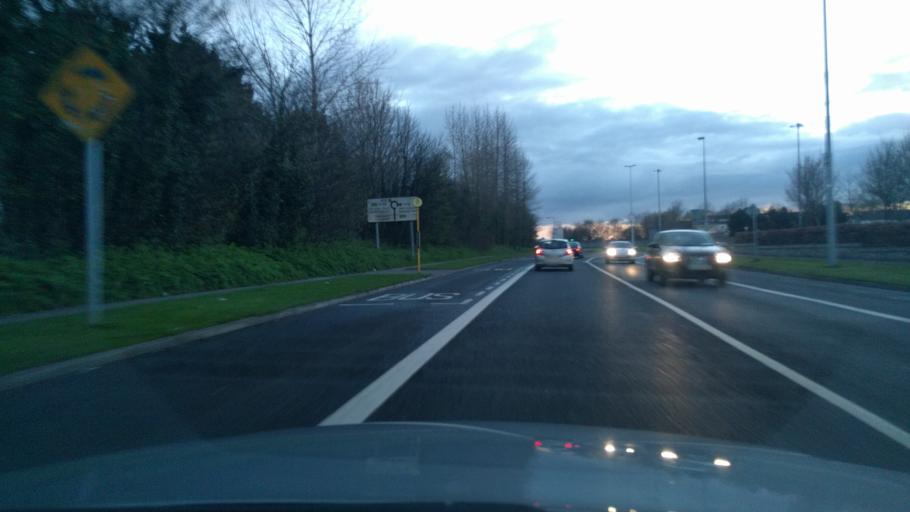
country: IE
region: Leinster
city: Clondalkin
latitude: 53.3250
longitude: -6.4030
